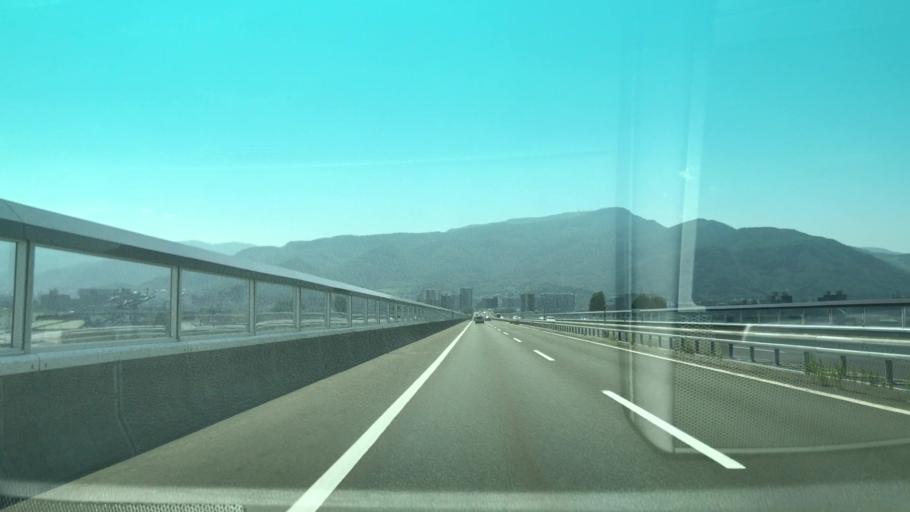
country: JP
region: Hokkaido
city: Sapporo
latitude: 43.0970
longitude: 141.2966
